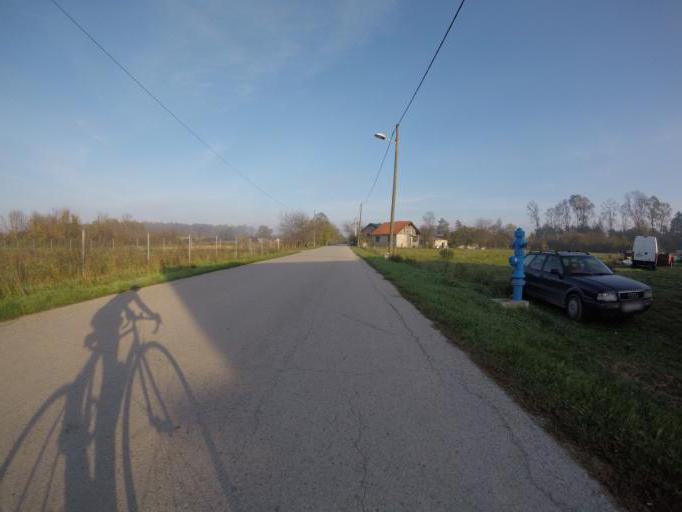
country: HR
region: Zagrebacka
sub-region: Grad Velika Gorica
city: Velika Gorica
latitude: 45.7269
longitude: 16.1150
